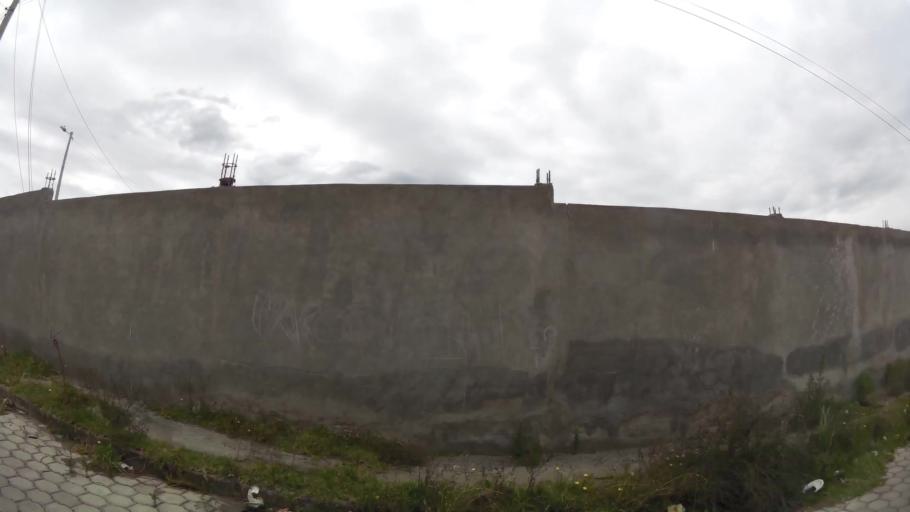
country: EC
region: Cotopaxi
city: Latacunga
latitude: -0.9585
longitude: -78.6081
